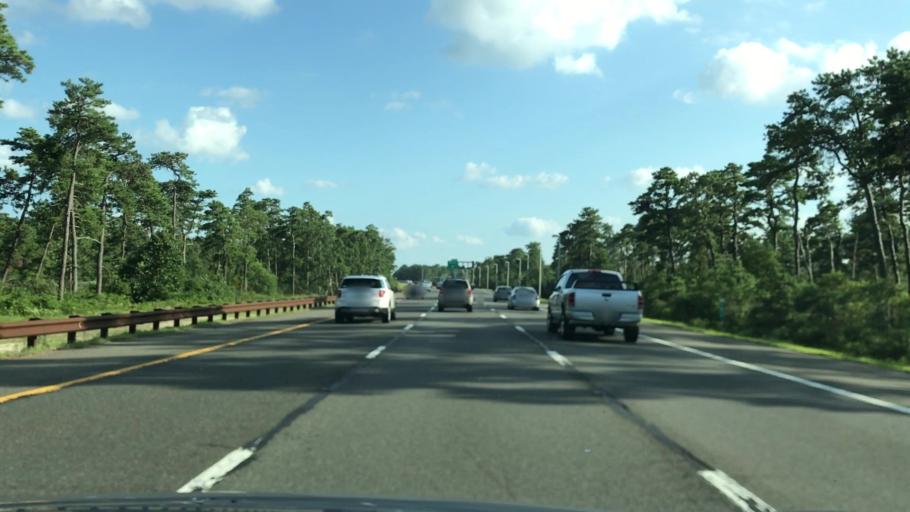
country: US
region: New Jersey
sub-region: Ocean County
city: South Toms River
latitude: 39.9122
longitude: -74.2123
